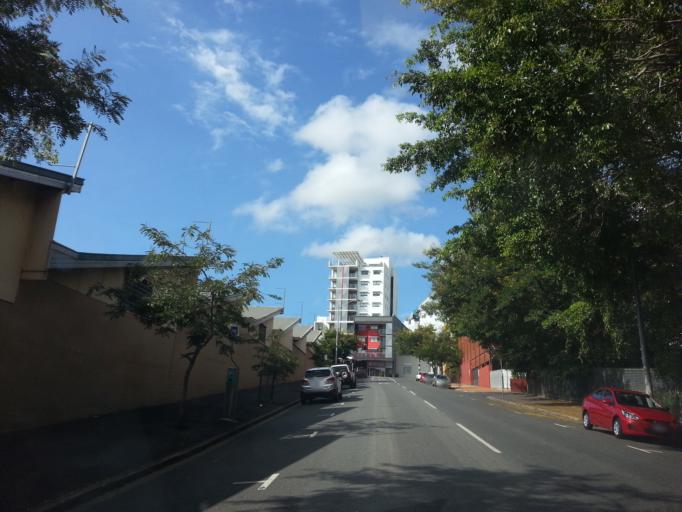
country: AU
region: Queensland
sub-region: Brisbane
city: Fortitude Valley
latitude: -27.4504
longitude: 153.0342
